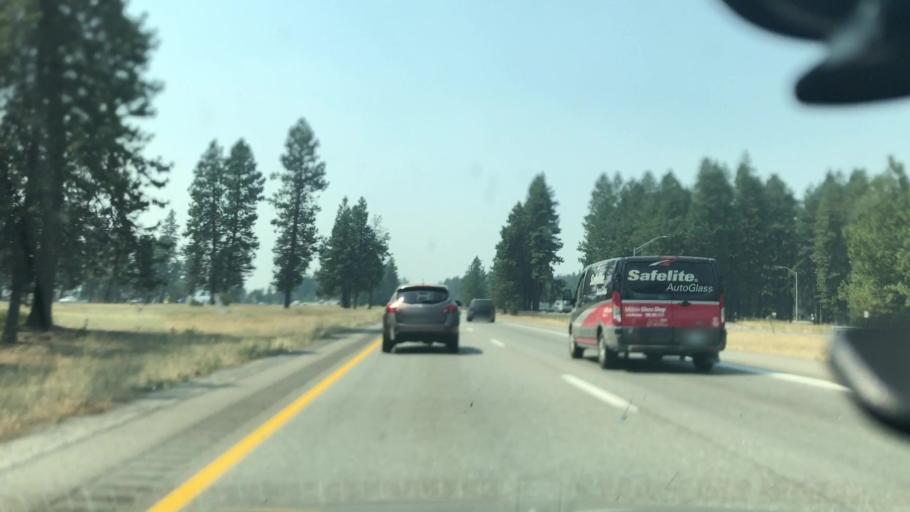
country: US
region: Idaho
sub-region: Kootenai County
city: Coeur d'Alene
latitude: 47.7092
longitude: -116.8627
